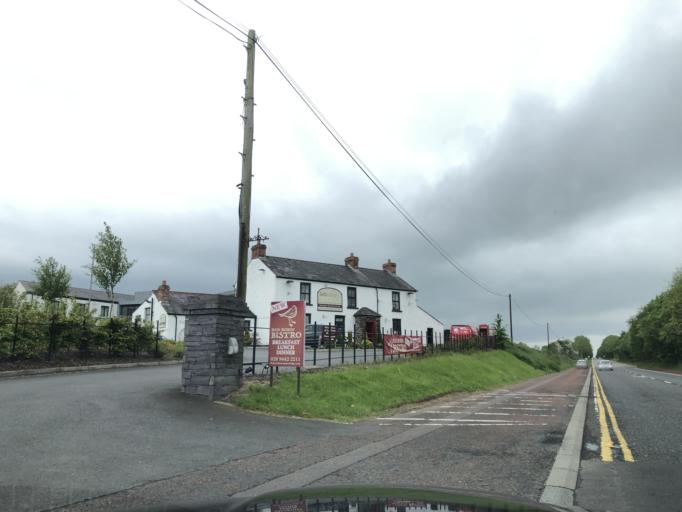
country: GB
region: Northern Ireland
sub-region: Antrim Borough
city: Antrim
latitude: 54.6674
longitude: -6.1929
